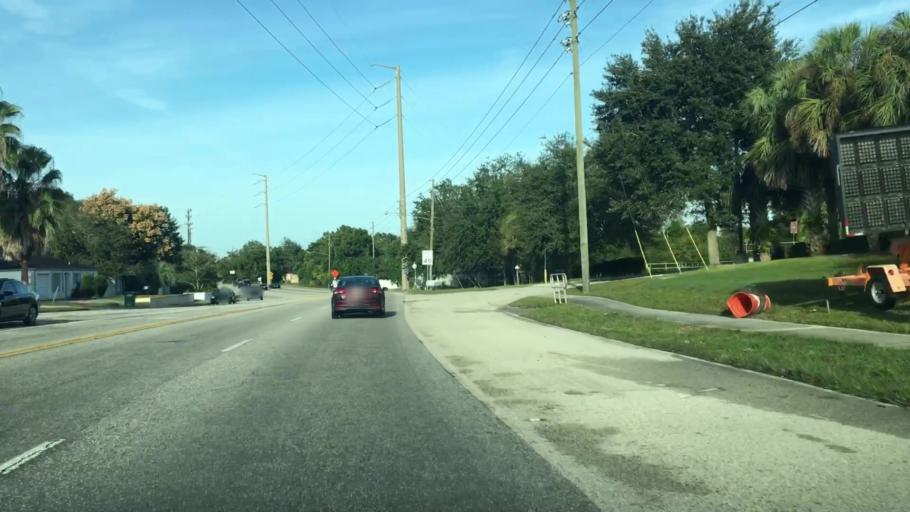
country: US
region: Florida
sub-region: Volusia County
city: Deltona
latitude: 28.9105
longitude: -81.2602
